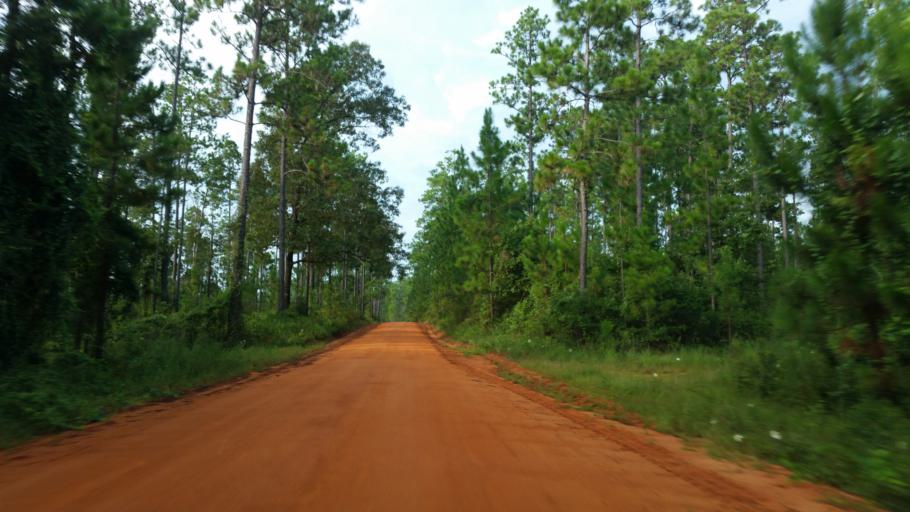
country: US
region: Alabama
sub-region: Escambia County
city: Atmore
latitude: 30.8821
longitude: -87.5823
